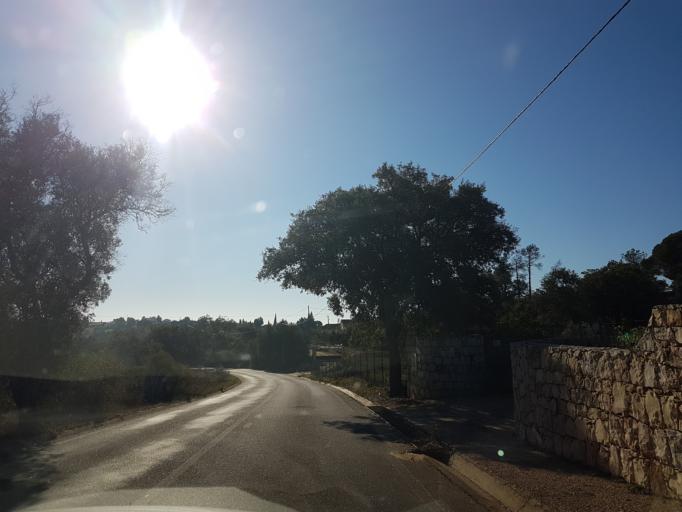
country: PT
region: Faro
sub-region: Lagoa
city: Carvoeiro
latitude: 37.1055
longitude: -8.4305
